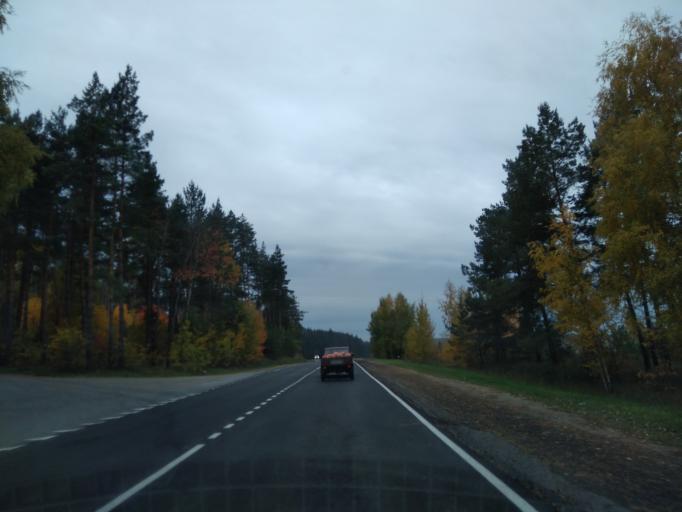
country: RU
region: Lipetsk
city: Zadonsk
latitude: 52.3643
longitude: 38.9160
